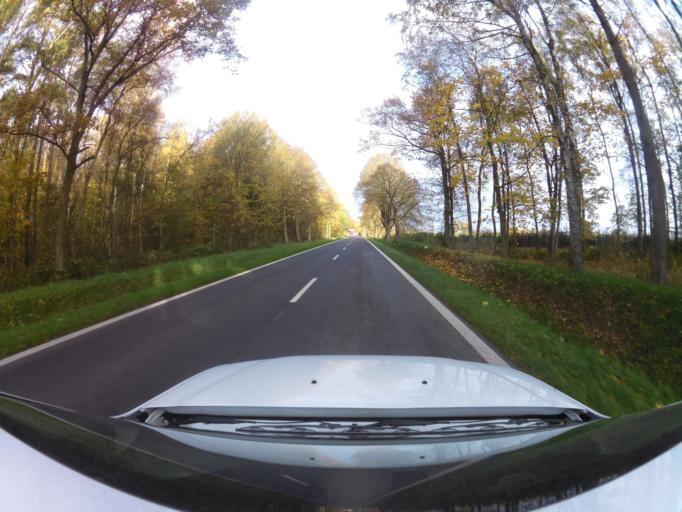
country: PL
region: West Pomeranian Voivodeship
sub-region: Powiat gryficki
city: Trzebiatow
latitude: 53.9936
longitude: 15.2396
